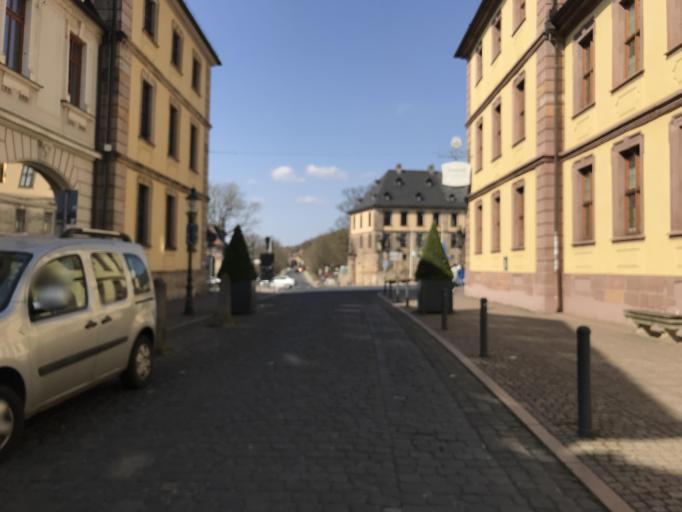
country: DE
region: Hesse
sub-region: Regierungsbezirk Kassel
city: Fulda
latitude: 50.5524
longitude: 9.6755
